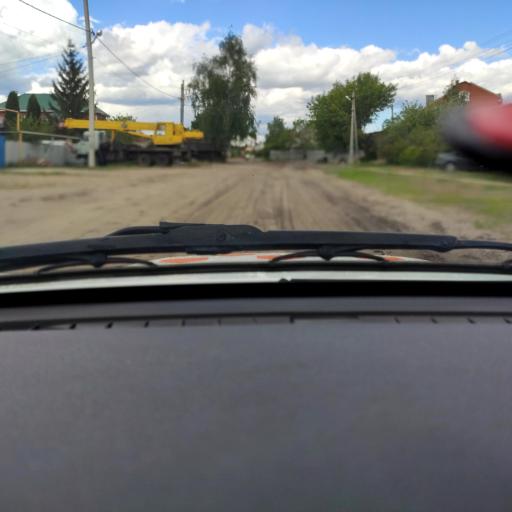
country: RU
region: Voronezj
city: Podgornoye
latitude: 51.7421
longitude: 39.1577
